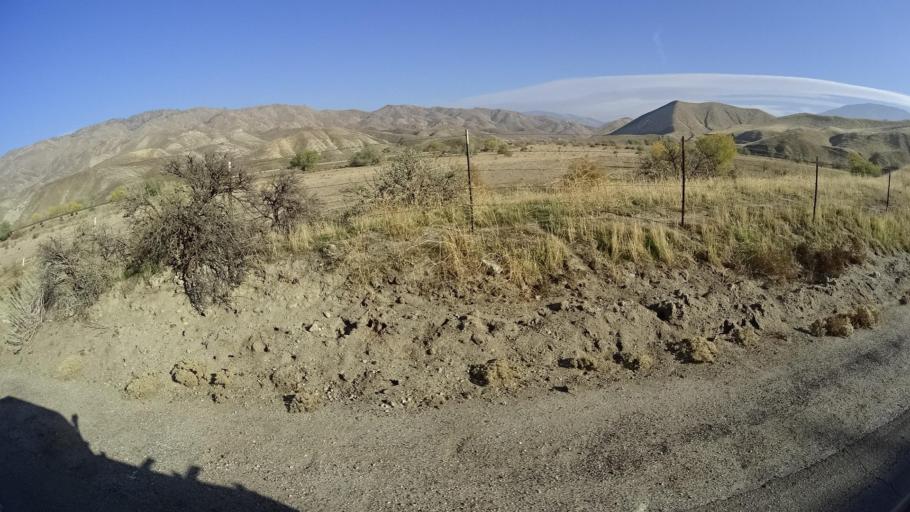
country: US
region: California
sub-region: Kern County
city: Arvin
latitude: 35.3136
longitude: -118.7048
